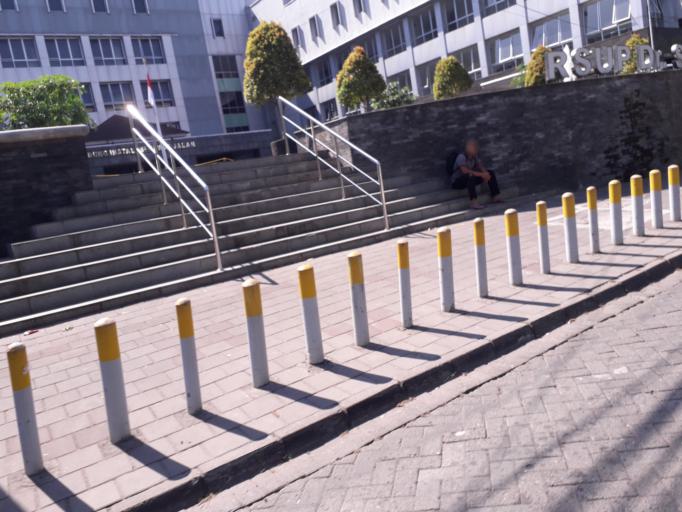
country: ID
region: Daerah Istimewa Yogyakarta
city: Yogyakarta
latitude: -7.7683
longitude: 110.3741
